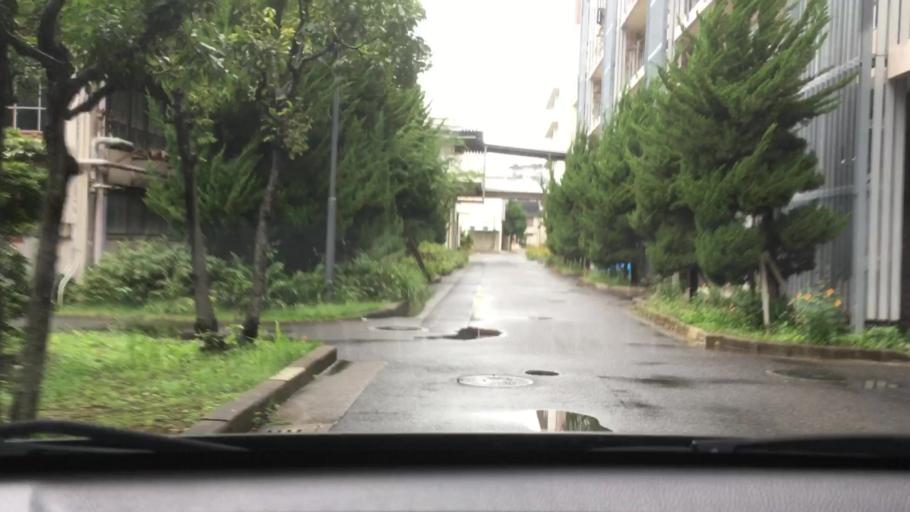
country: JP
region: Nagasaki
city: Obita
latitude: 32.7862
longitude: 129.8637
